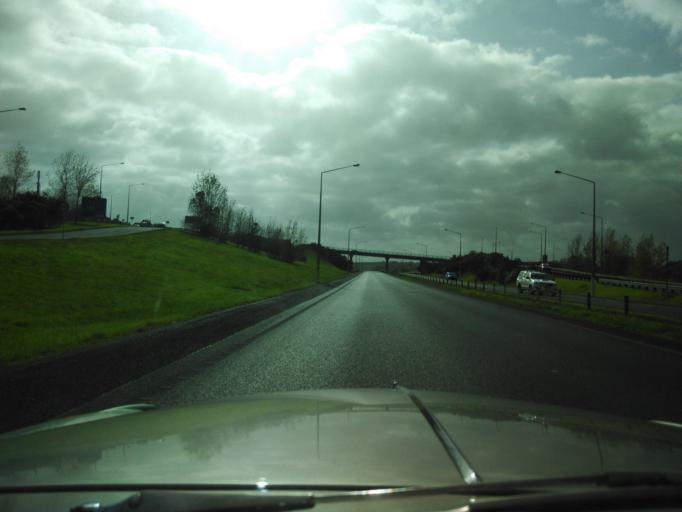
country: NZ
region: Auckland
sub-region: Auckland
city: Rothesay Bay
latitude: -36.6275
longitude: 174.6627
